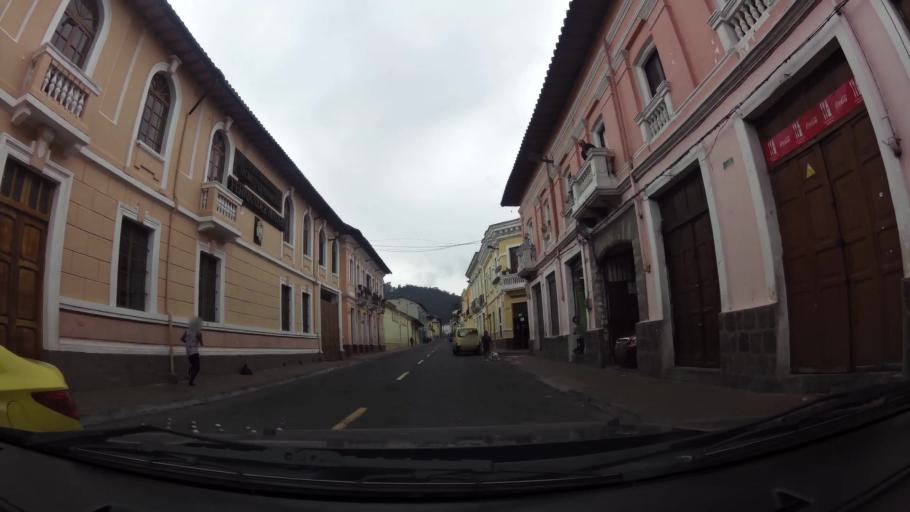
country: EC
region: Pichincha
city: Quito
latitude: -0.2266
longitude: -78.5108
